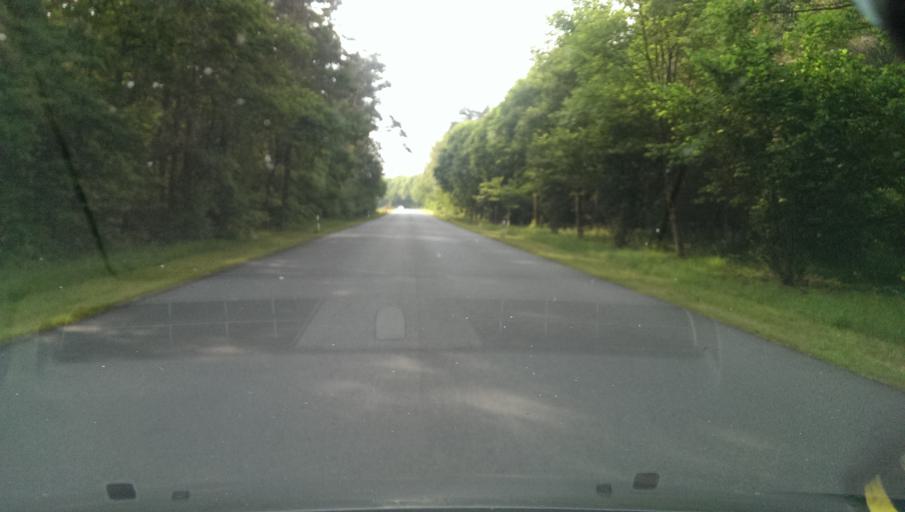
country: DE
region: Lower Saxony
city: Munster
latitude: 52.9155
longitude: 10.0790
